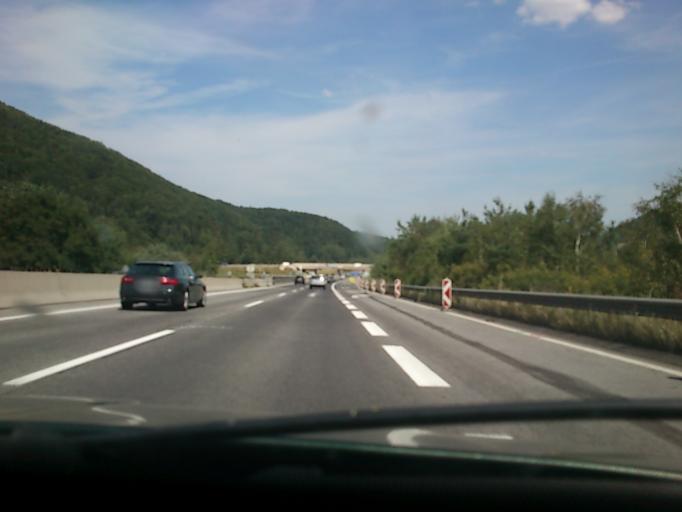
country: AT
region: Lower Austria
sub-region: Politischer Bezirk Neunkirchen
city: Grimmenstein
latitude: 47.6283
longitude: 16.1310
